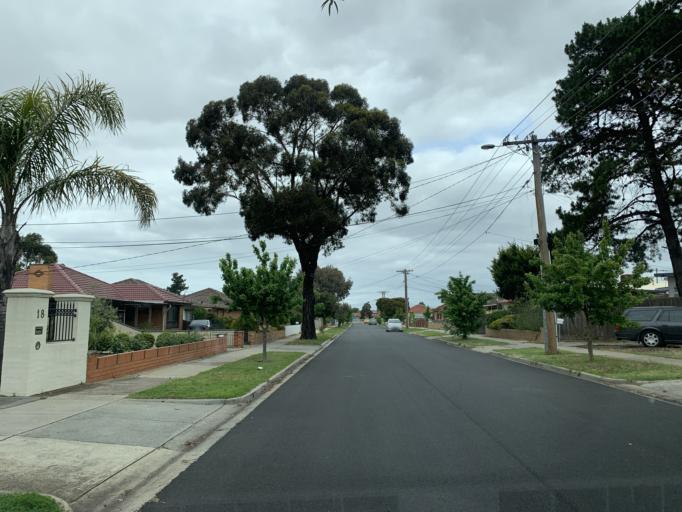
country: AU
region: Victoria
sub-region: Brimbank
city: St Albans
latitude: -37.7443
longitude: 144.8148
